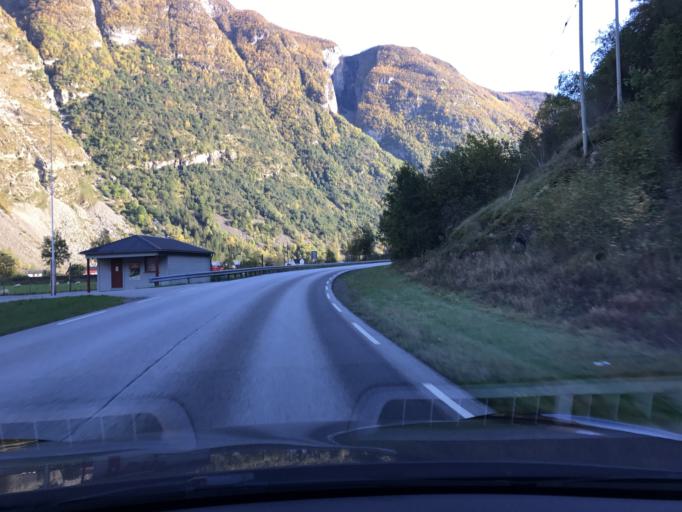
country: NO
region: Sogn og Fjordane
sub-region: Laerdal
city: Laerdalsoyri
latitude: 61.0977
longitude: 7.5162
